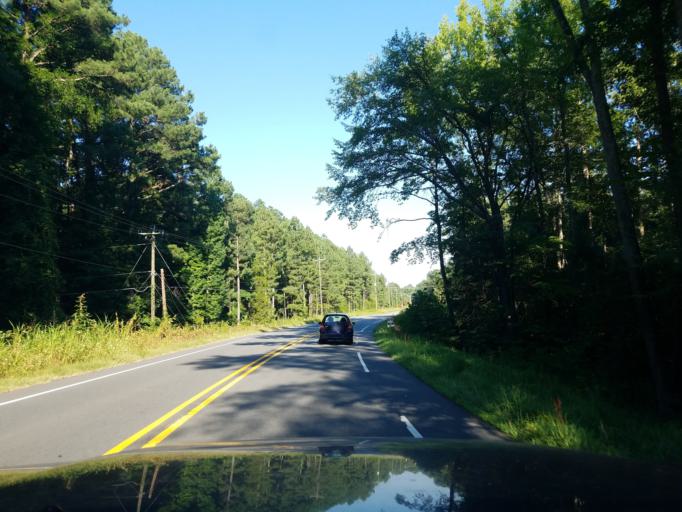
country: US
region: North Carolina
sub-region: Orange County
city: Chapel Hill
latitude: 35.8893
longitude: -78.9933
